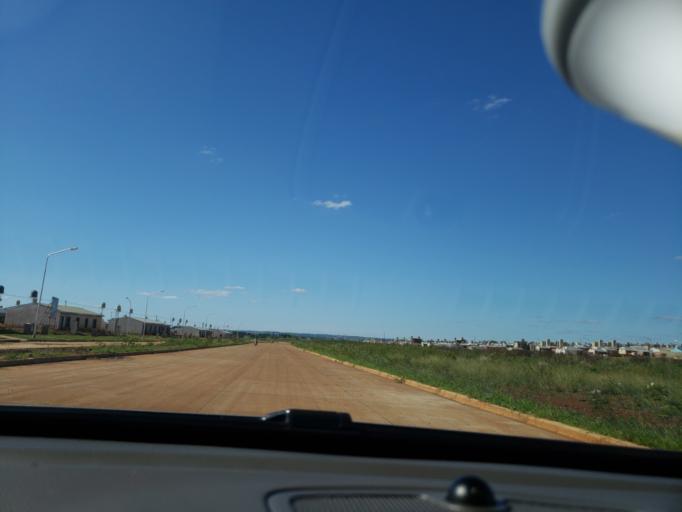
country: AR
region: Misiones
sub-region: Departamento de Capital
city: Posadas
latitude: -27.4067
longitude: -55.9887
